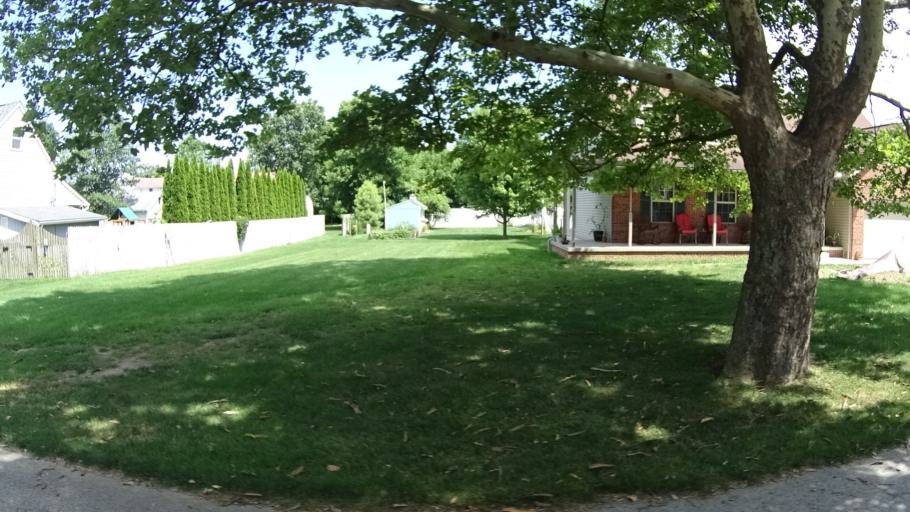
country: US
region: Ohio
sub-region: Erie County
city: Sandusky
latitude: 41.3964
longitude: -82.8058
